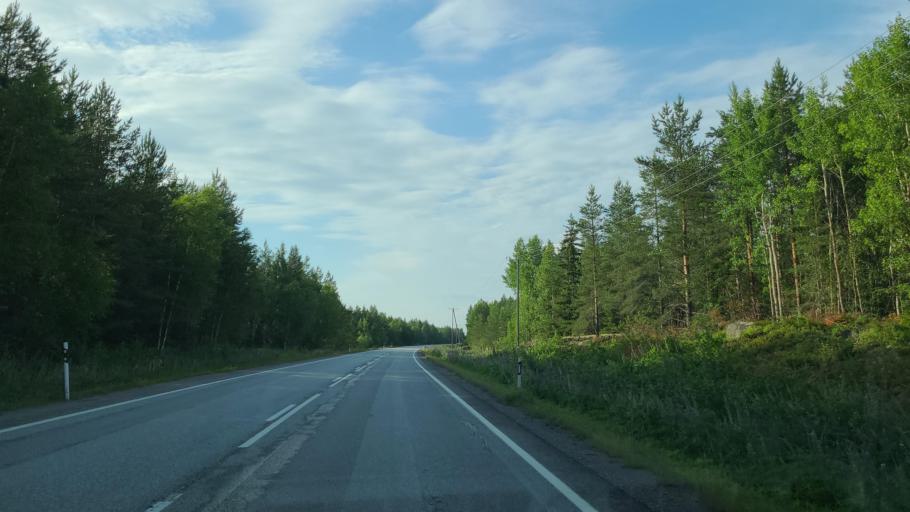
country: FI
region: Ostrobothnia
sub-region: Vaasa
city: Vaasa
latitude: 63.1570
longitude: 21.5943
